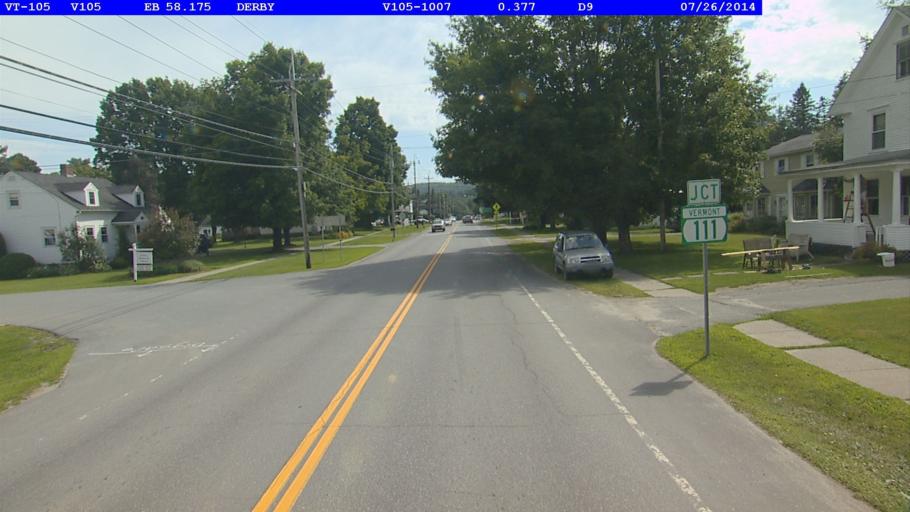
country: US
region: Vermont
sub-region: Orleans County
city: Newport
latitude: 44.9492
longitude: -72.1329
